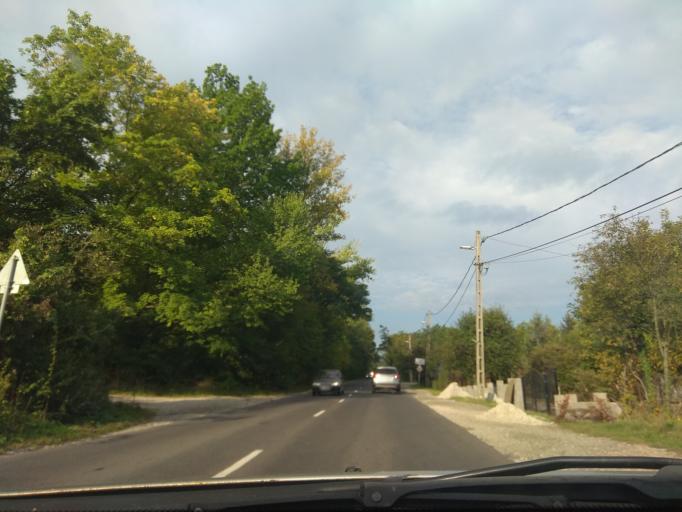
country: HU
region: Borsod-Abauj-Zemplen
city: Miskolc
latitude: 48.0906
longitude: 20.7599
